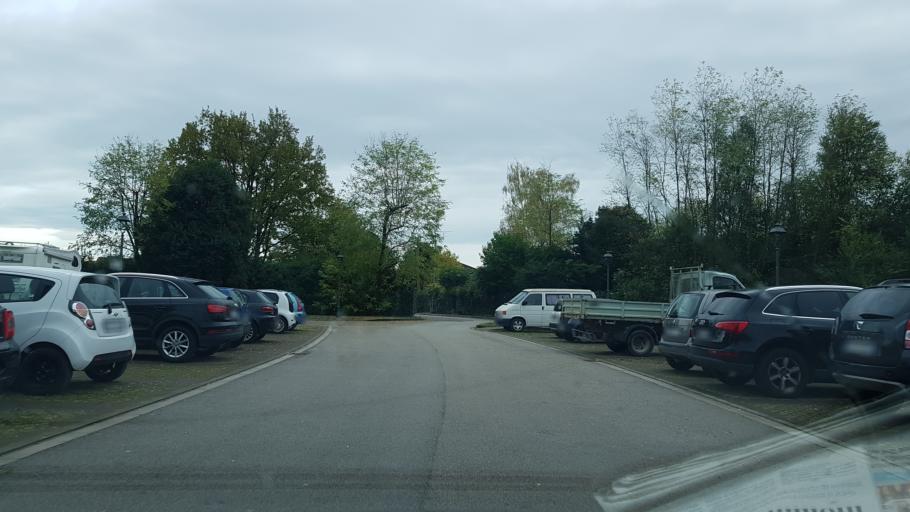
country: IT
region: Friuli Venezia Giulia
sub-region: Provincia di Gorizia
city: San Pier d'Isonzo
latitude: 45.8467
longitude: 13.4591
